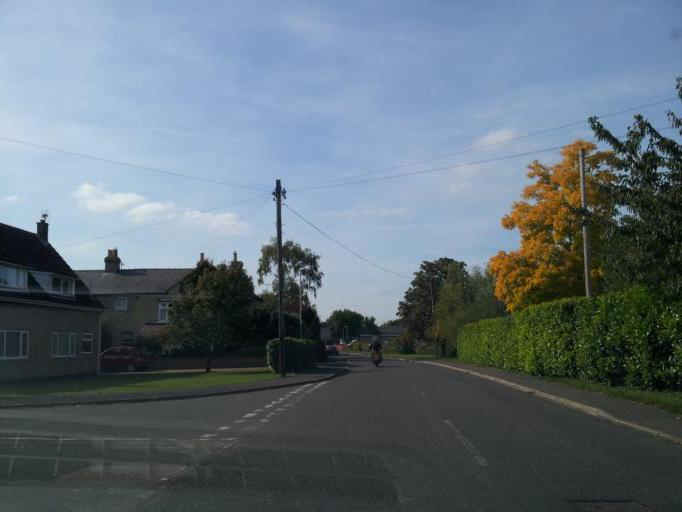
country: GB
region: England
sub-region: Cambridgeshire
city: Waterbeach
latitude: 52.2645
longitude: 0.1646
